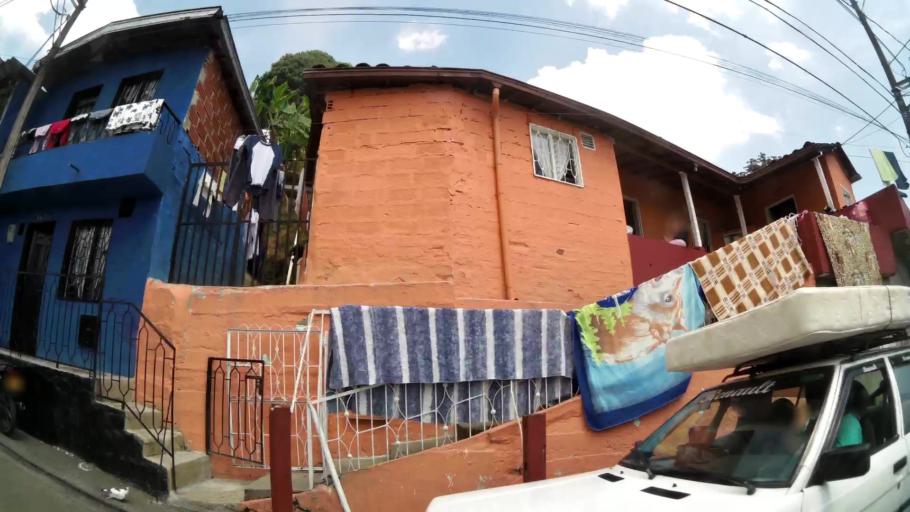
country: CO
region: Antioquia
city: La Estrella
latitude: 6.1823
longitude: -75.6610
